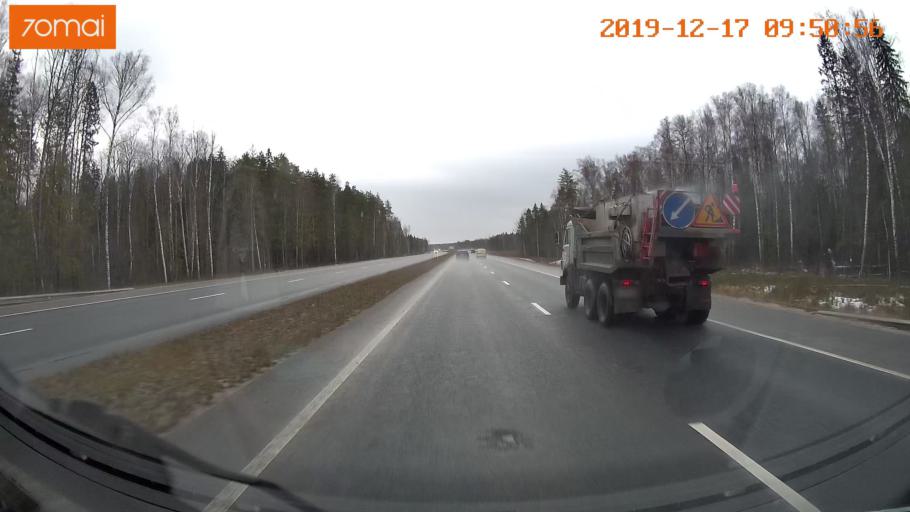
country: RU
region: Vladimir
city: Kommunar
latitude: 56.0512
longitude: 40.5151
